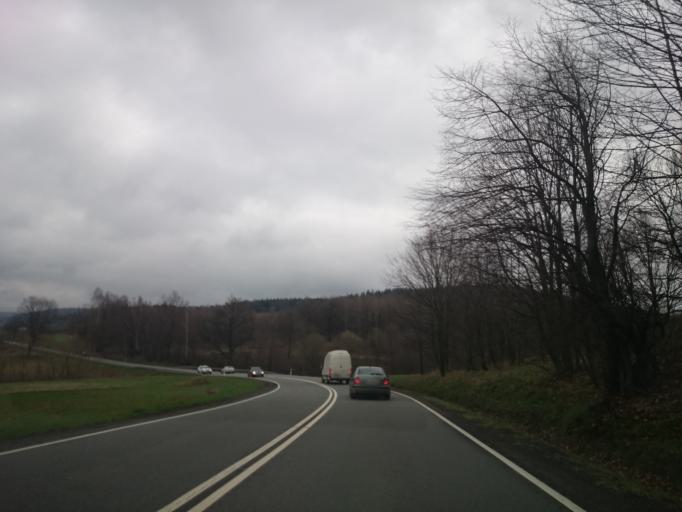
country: PL
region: Lower Silesian Voivodeship
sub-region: Powiat zabkowicki
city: Zloty Stok
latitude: 50.4512
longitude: 16.8535
